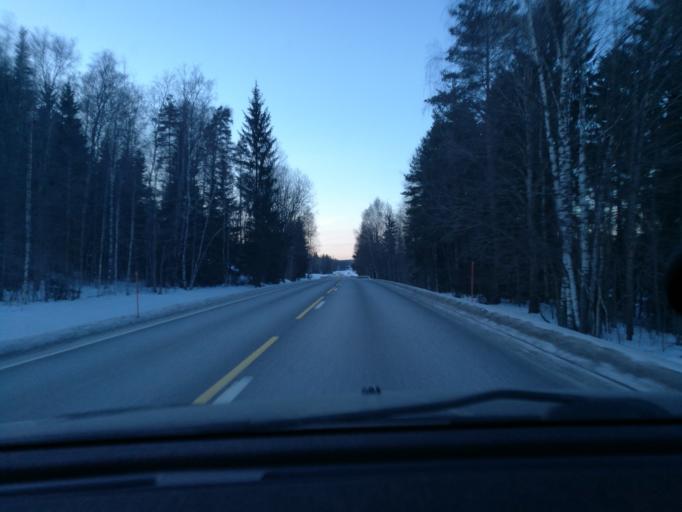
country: FI
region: Uusimaa
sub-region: Helsinki
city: Vihti
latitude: 60.4260
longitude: 24.4331
